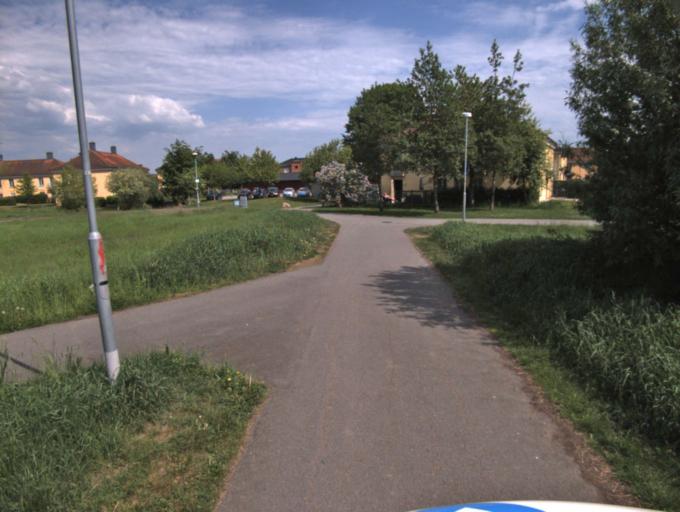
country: SE
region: Skane
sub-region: Kristianstads Kommun
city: Kristianstad
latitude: 56.0511
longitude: 14.1479
